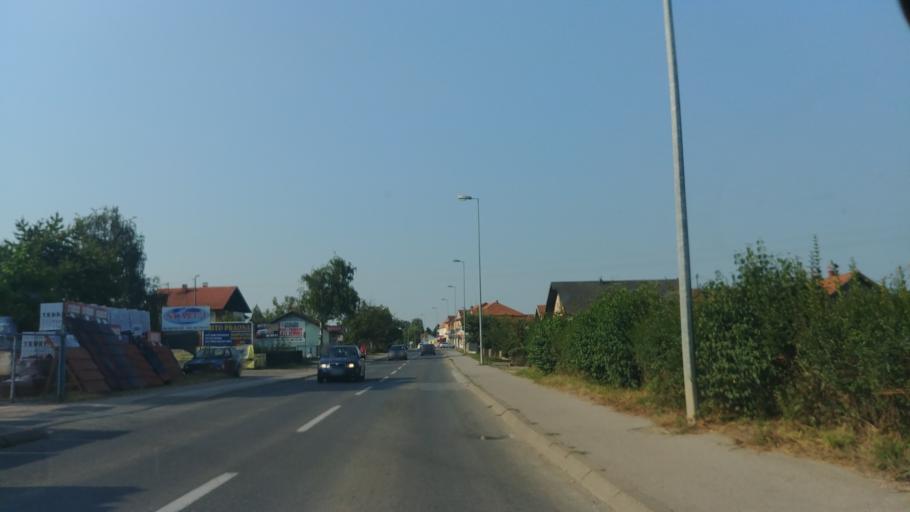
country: BA
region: Brcko
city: Brcko
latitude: 44.8536
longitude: 18.8143
